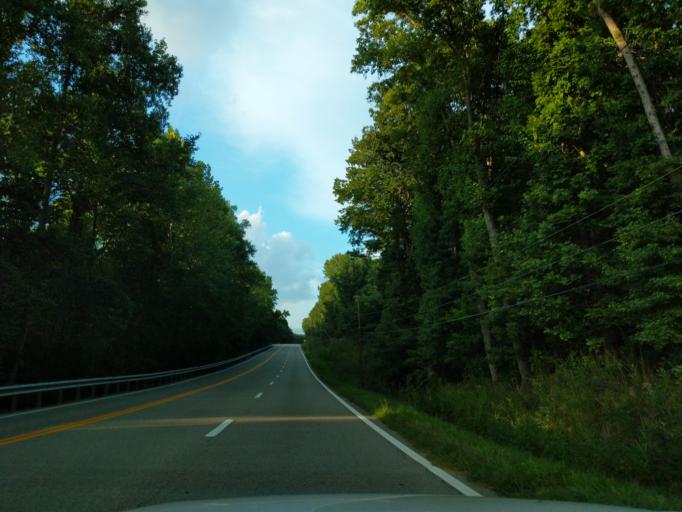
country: US
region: Tennessee
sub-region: Marion County
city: Jasper
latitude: 35.0489
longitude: -85.5306
